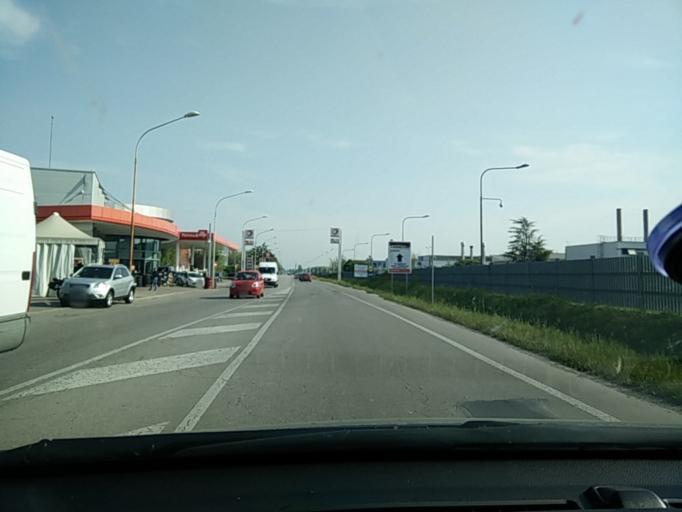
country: IT
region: Friuli Venezia Giulia
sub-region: Provincia di Pordenone
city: Azzano Decimo
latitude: 45.9293
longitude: 12.6447
